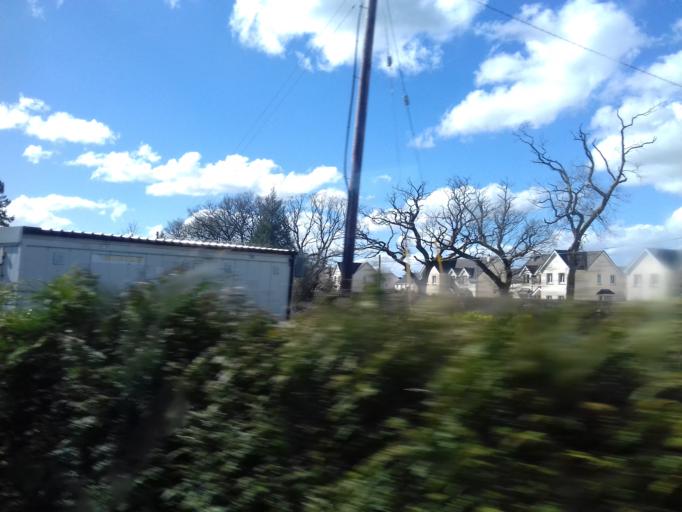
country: IE
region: Munster
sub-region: County Cork
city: Millstreet
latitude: 52.0958
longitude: -8.9751
